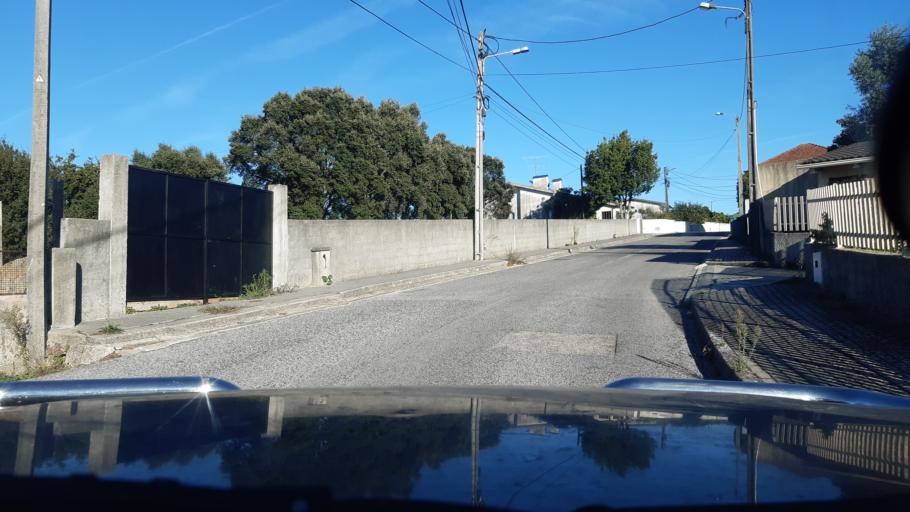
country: PT
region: Aveiro
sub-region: Agueda
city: Agueda
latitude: 40.5563
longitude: -8.4389
